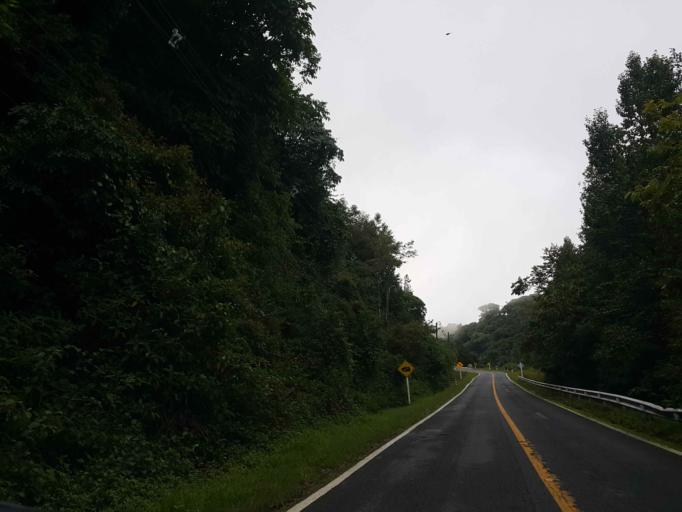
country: TH
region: Chiang Mai
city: Mae Chaem
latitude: 18.5676
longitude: 98.4844
